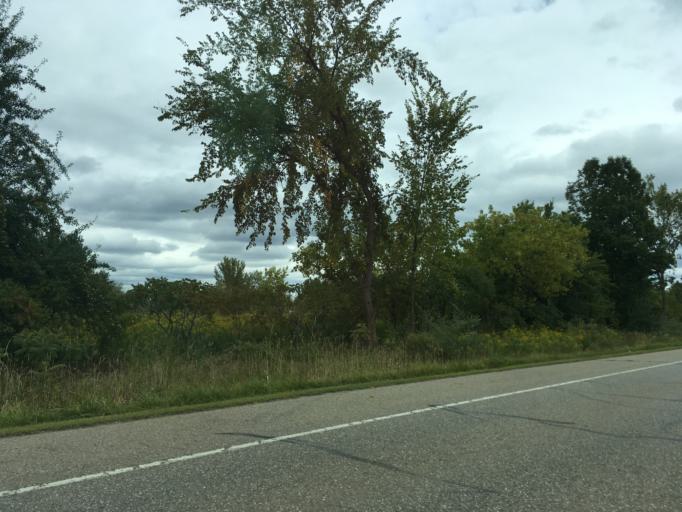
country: US
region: Michigan
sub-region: Tuscola County
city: Caro
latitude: 43.3366
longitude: -83.3645
